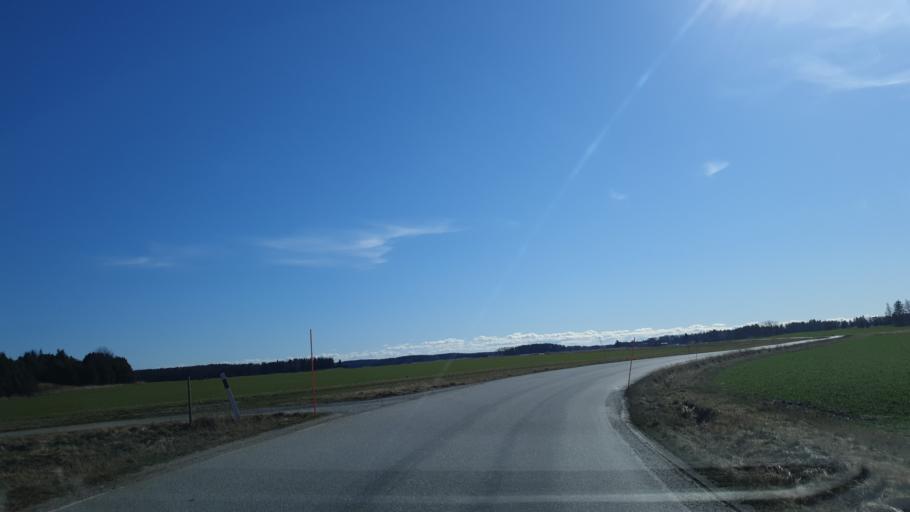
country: SE
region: Uppsala
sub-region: Enkopings Kommun
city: Grillby
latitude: 59.6021
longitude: 17.2727
